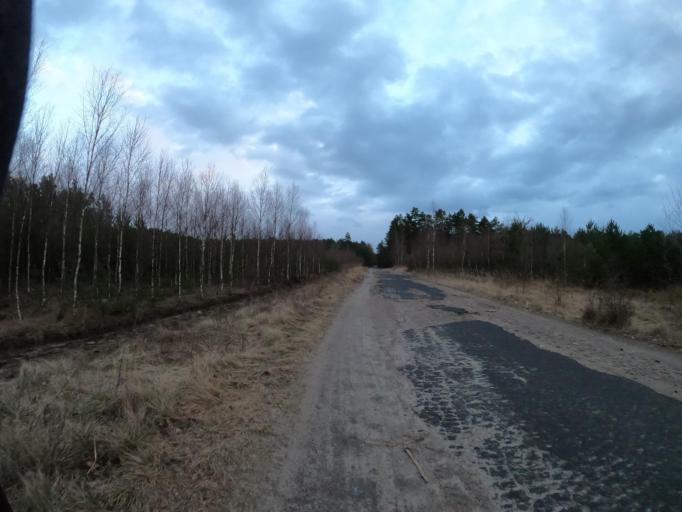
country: PL
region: West Pomeranian Voivodeship
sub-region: Powiat szczecinecki
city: Borne Sulinowo
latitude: 53.5476
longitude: 16.5826
